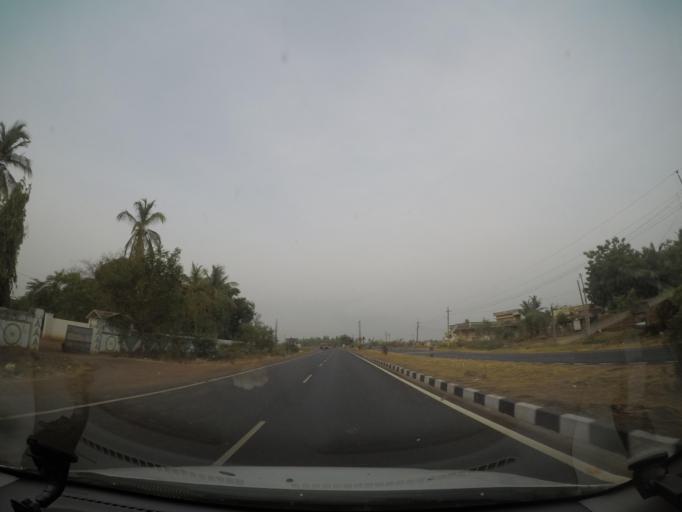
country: IN
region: Andhra Pradesh
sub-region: Krishna
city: Gannavaram
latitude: 16.6073
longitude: 80.9050
